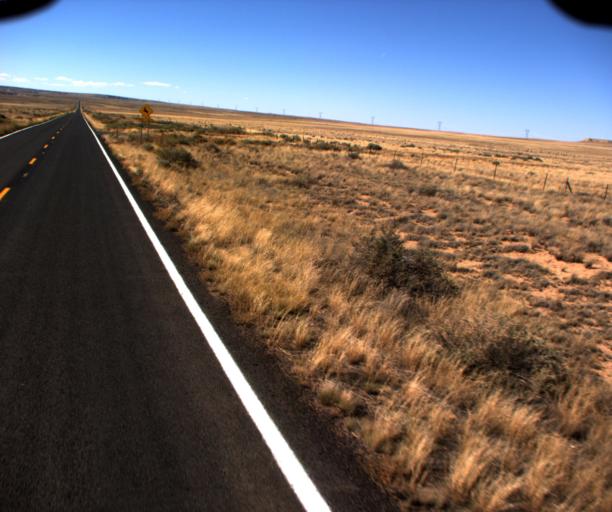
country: US
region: Arizona
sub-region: Navajo County
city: First Mesa
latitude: 35.9749
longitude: -110.7662
